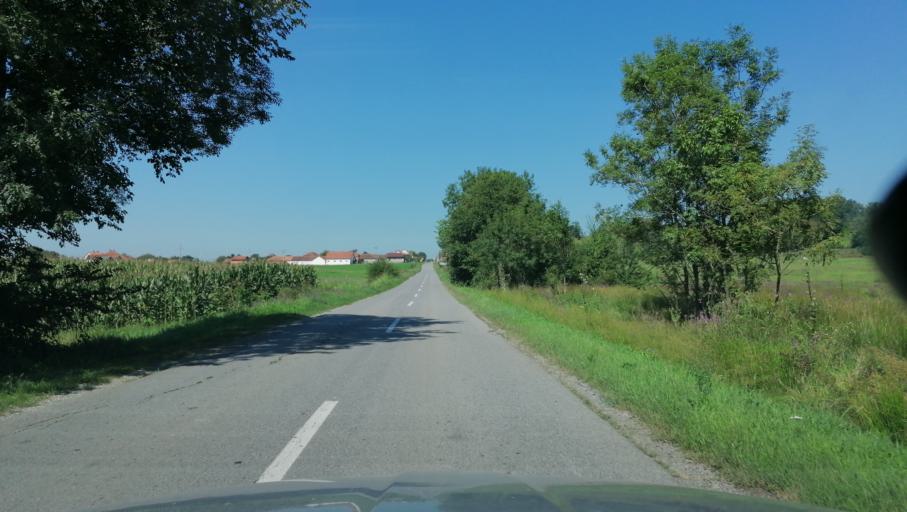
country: RS
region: Central Serbia
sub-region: Raski Okrug
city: Vrnjacka Banja
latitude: 43.6847
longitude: 20.8830
